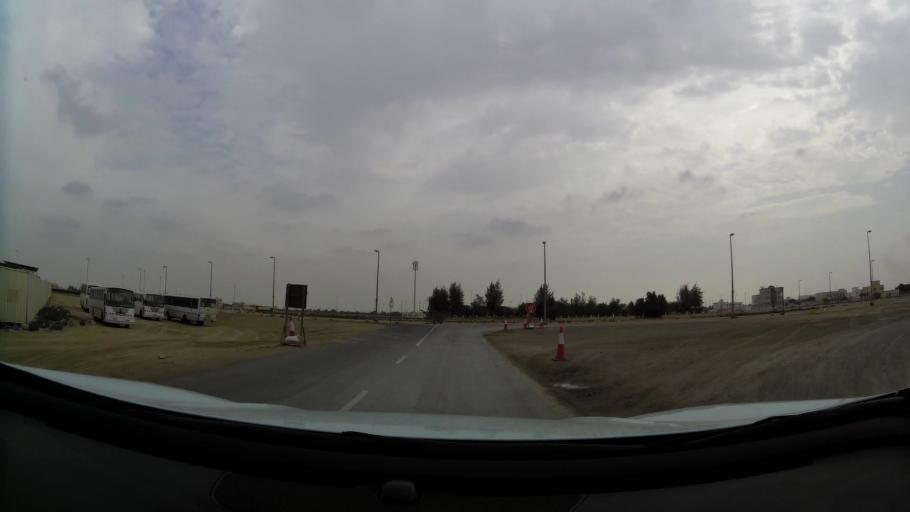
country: AE
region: Abu Dhabi
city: Abu Dhabi
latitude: 24.6225
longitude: 54.7084
